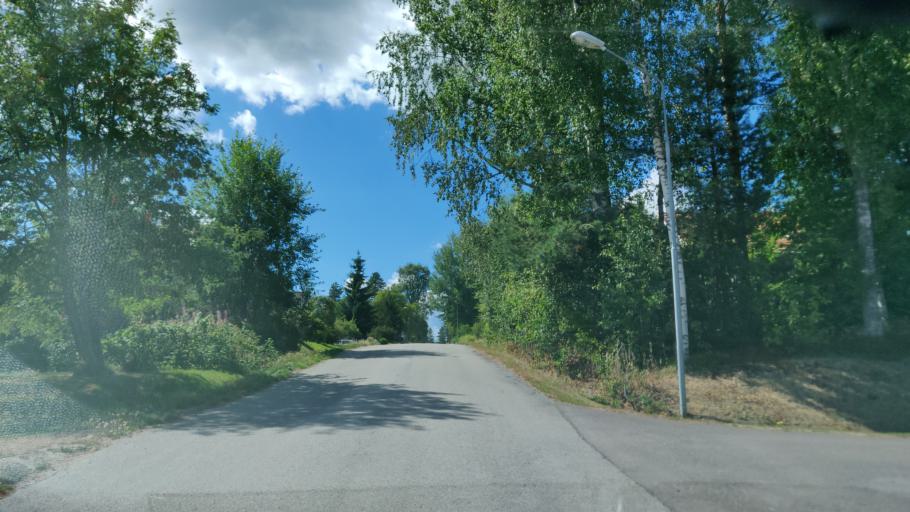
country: SE
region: Vaermland
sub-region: Hagfors Kommun
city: Ekshaerad
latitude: 60.1801
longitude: 13.4945
